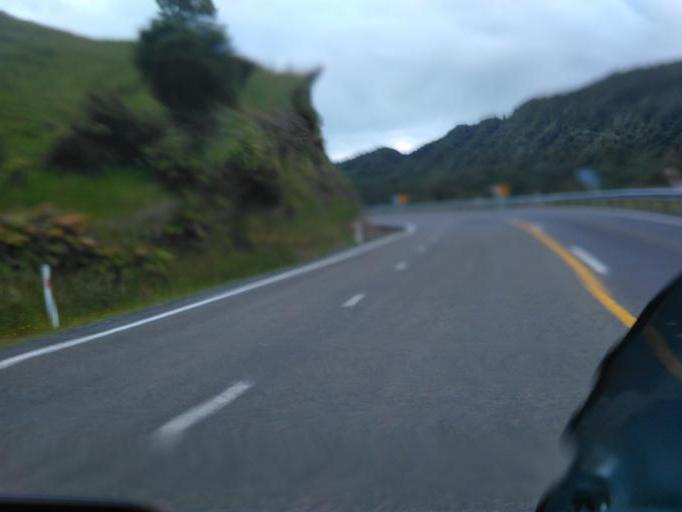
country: NZ
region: Bay of Plenty
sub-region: Opotiki District
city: Opotiki
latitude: -38.3533
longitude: 177.4505
